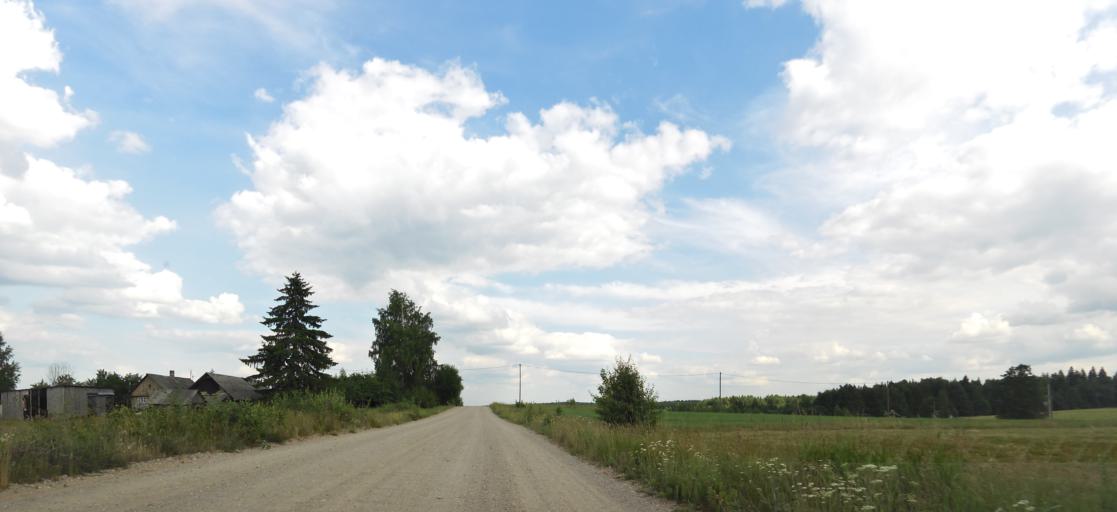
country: LT
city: Skaidiskes
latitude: 54.5308
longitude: 25.6351
